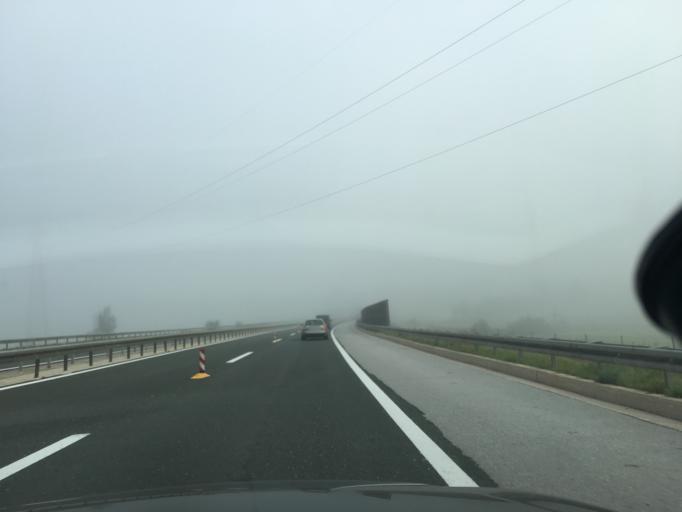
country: HR
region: Licko-Senjska
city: Otocac
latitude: 44.8658
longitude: 15.2084
